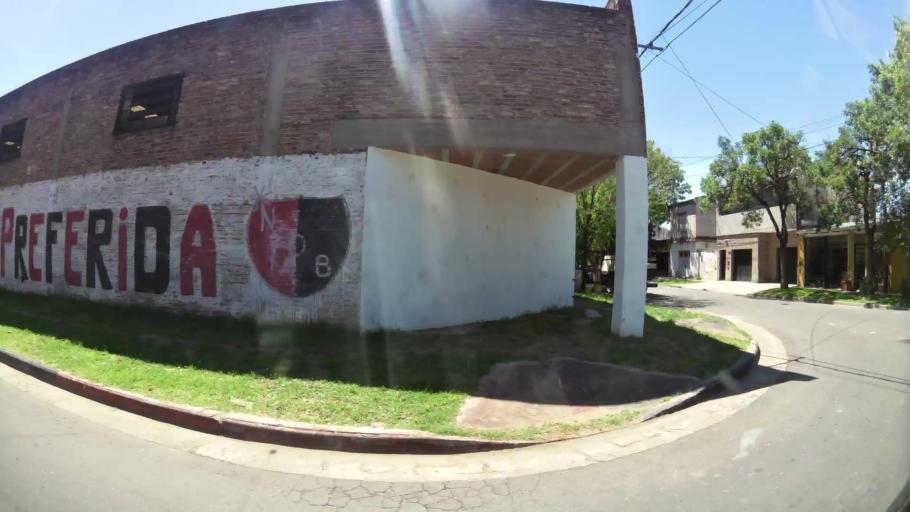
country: AR
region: Santa Fe
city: Perez
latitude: -32.9548
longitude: -60.7108
